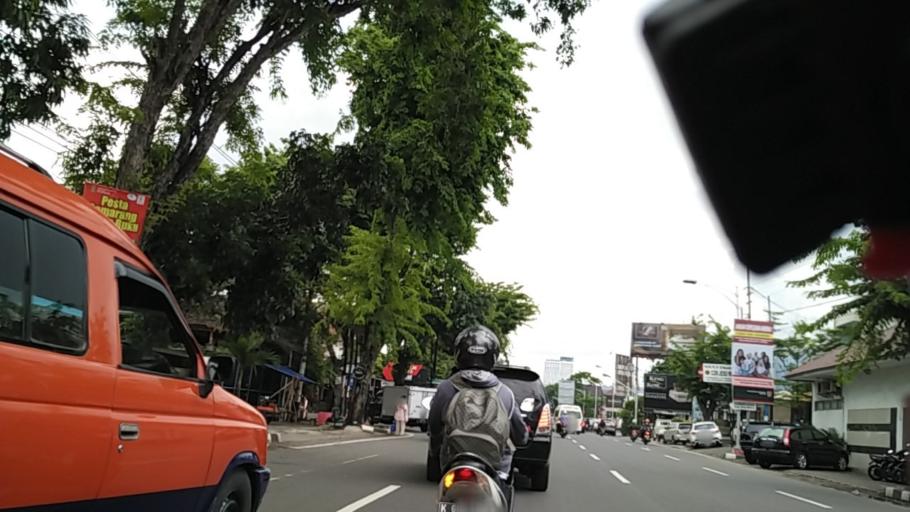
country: ID
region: Central Java
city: Semarang
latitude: -6.9933
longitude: 110.4341
